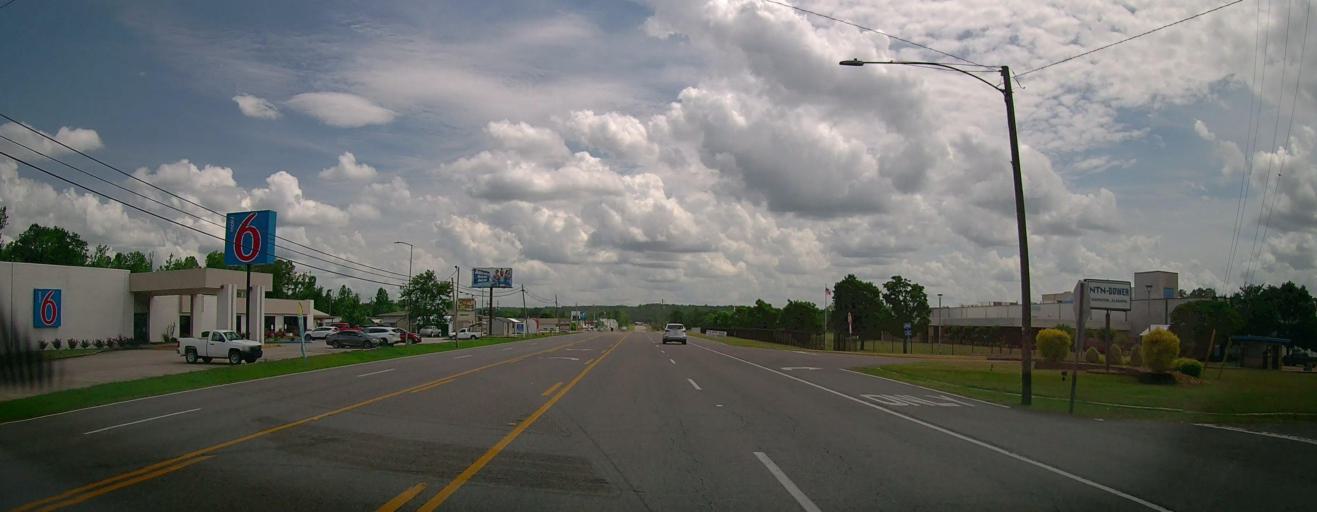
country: US
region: Alabama
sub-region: Marion County
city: Hamilton
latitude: 34.1153
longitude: -87.9895
